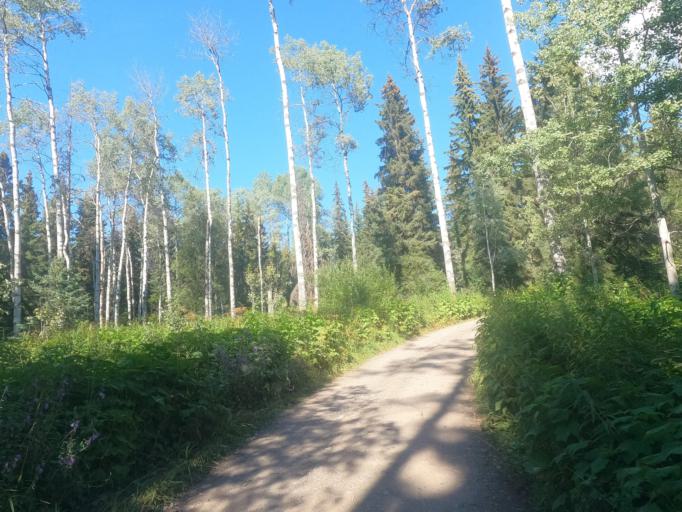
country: CA
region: British Columbia
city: Houston
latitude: 54.2861
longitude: -126.8514
